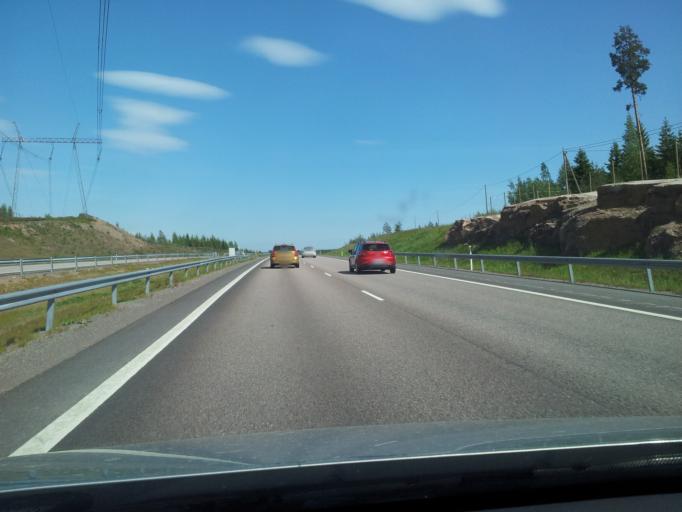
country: FI
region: Uusimaa
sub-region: Loviisa
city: Perna
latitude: 60.4785
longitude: 26.0871
